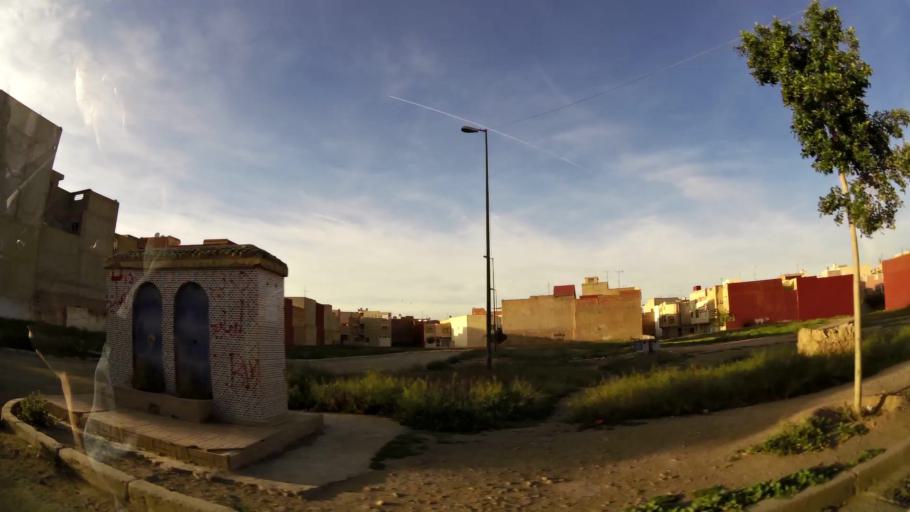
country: MA
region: Oriental
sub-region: Oujda-Angad
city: Oujda
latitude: 34.6753
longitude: -1.8969
